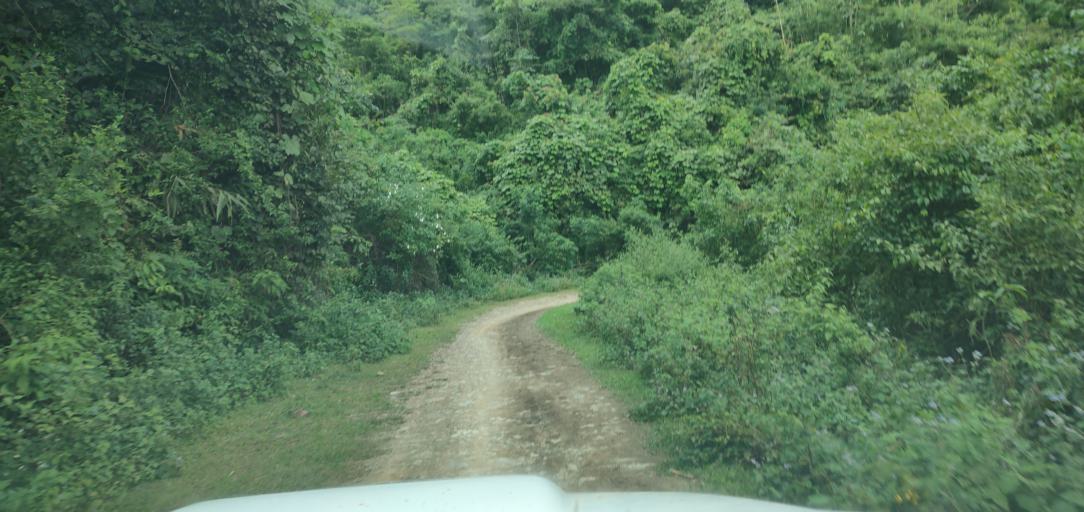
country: LA
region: Phongsali
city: Phongsali
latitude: 21.4471
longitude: 102.3134
